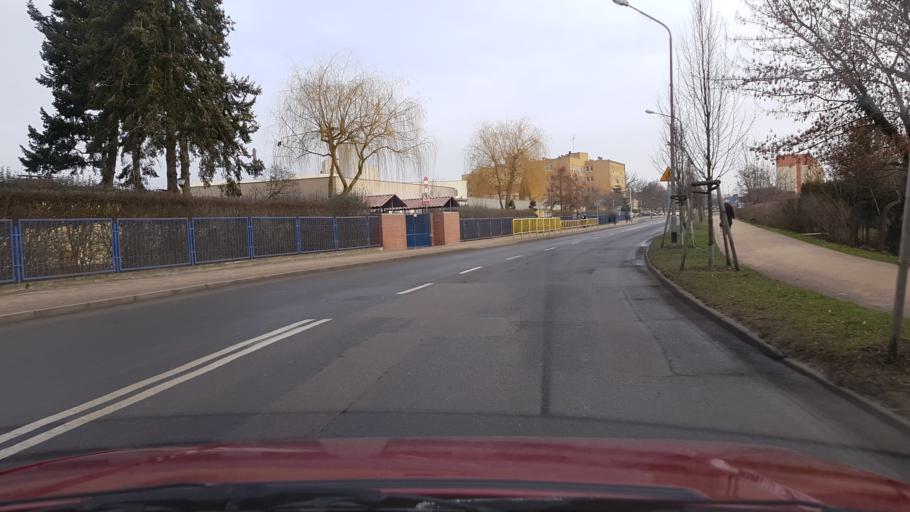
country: PL
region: West Pomeranian Voivodeship
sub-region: Powiat policki
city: Police
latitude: 53.5447
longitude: 14.5586
